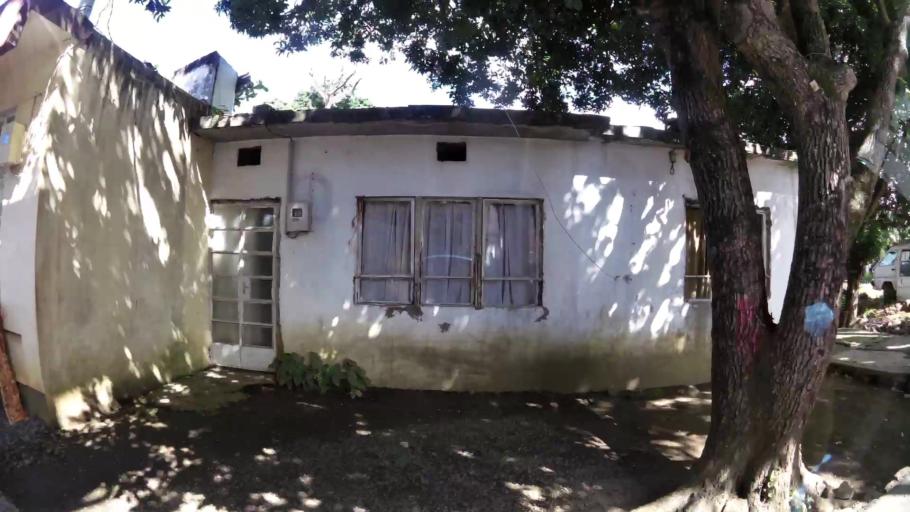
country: MU
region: Grand Port
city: Plaine Magnien
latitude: -20.4286
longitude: 57.6567
